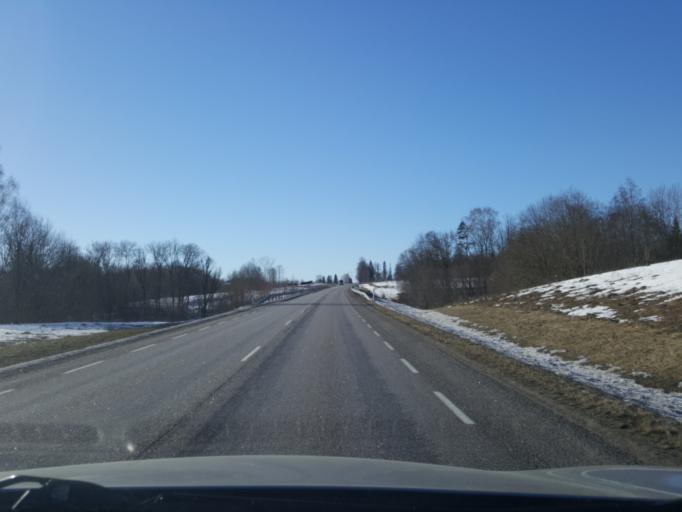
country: EE
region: Viljandimaa
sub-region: Viiratsi vald
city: Viiratsi
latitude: 58.4016
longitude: 25.6534
